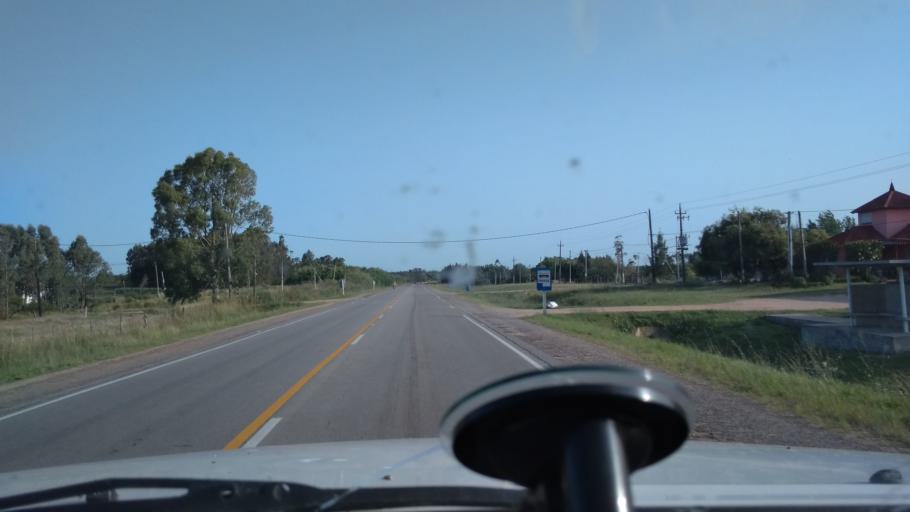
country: UY
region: Canelones
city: Santa Rosa
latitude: -34.5500
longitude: -56.0594
